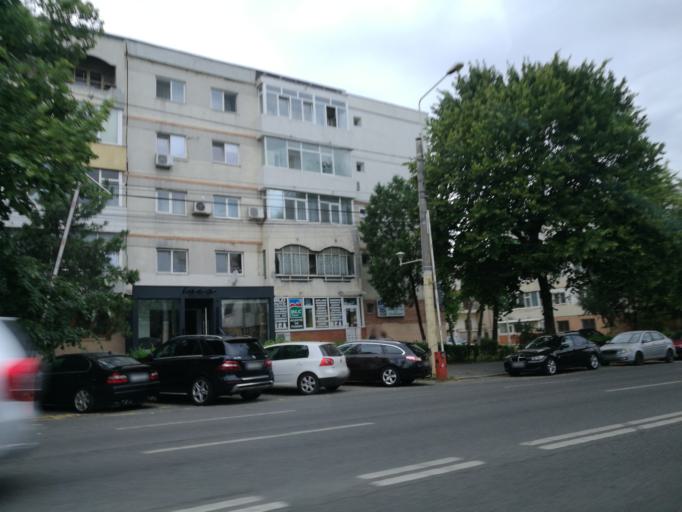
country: RO
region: Constanta
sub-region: Municipiul Constanta
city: Constanta
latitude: 44.1910
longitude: 28.6334
